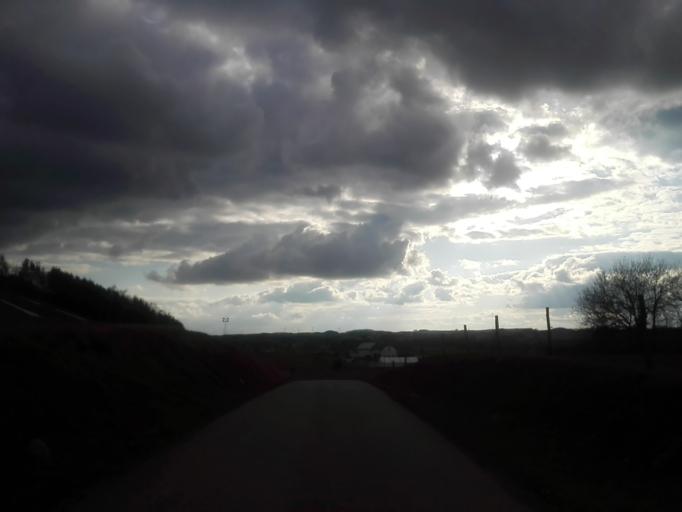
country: PL
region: Podlasie
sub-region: Suwalki
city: Suwalki
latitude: 54.2099
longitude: 22.9751
